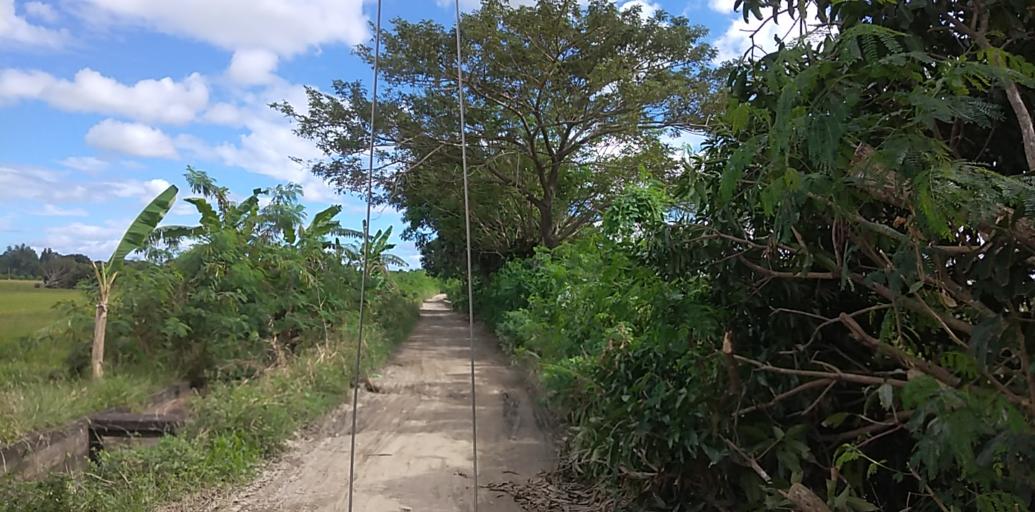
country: PH
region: Central Luzon
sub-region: Province of Pampanga
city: Santa Ana
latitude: 15.1188
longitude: 120.7767
